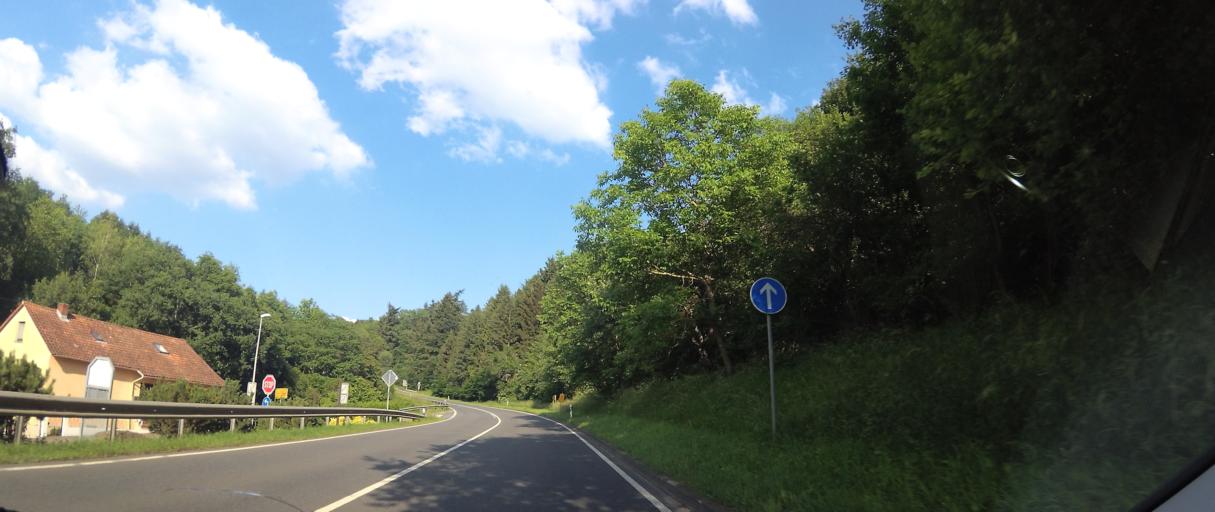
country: DE
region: Rheinland-Pfalz
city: Hochstatten
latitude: 49.7613
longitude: 7.8369
